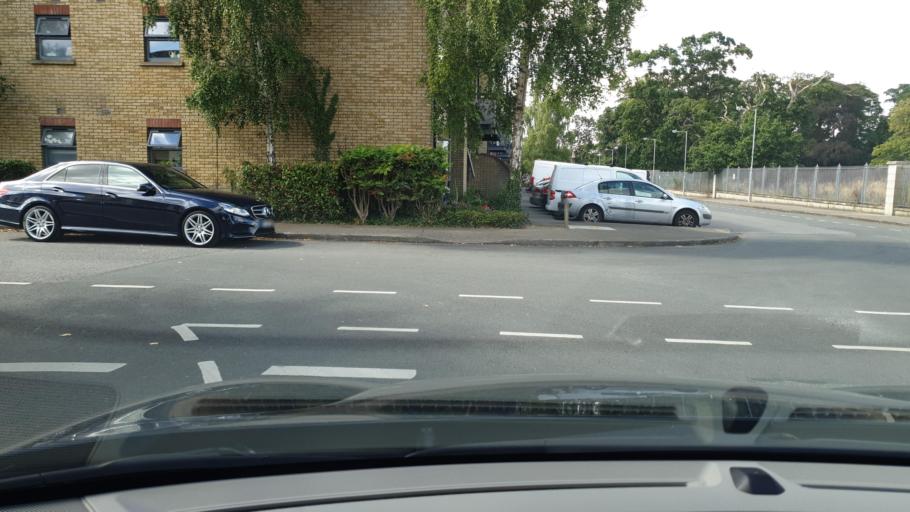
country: IE
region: Leinster
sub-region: An Mhi
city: Dunboyne
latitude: 53.4150
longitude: -6.4778
